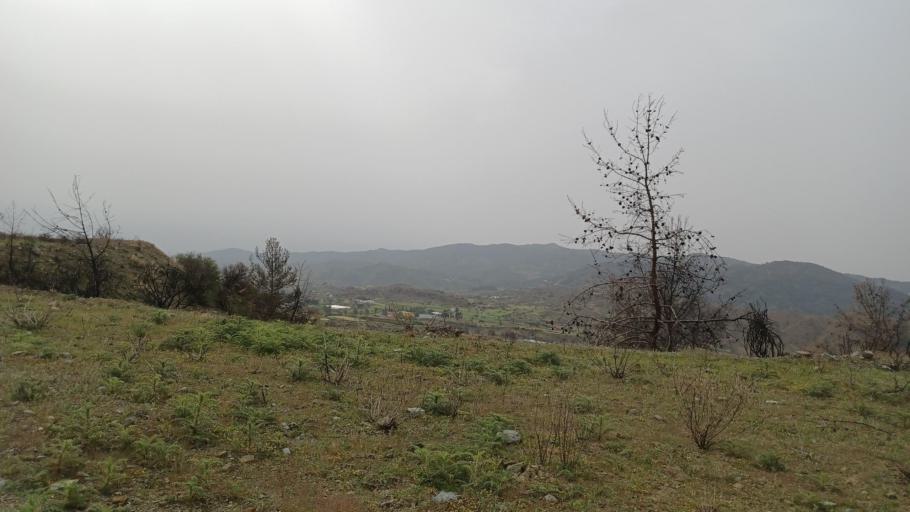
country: CY
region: Limassol
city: Parekklisha
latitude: 34.8549
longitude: 33.1335
